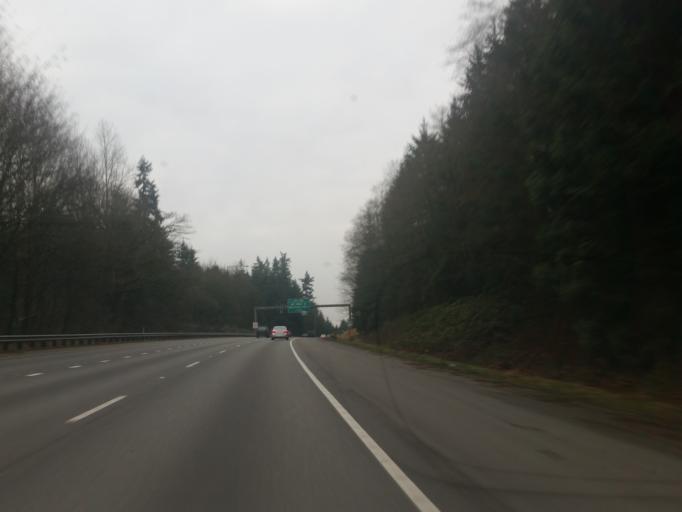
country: US
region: Washington
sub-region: King County
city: Bothell
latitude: 47.7862
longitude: -122.1986
